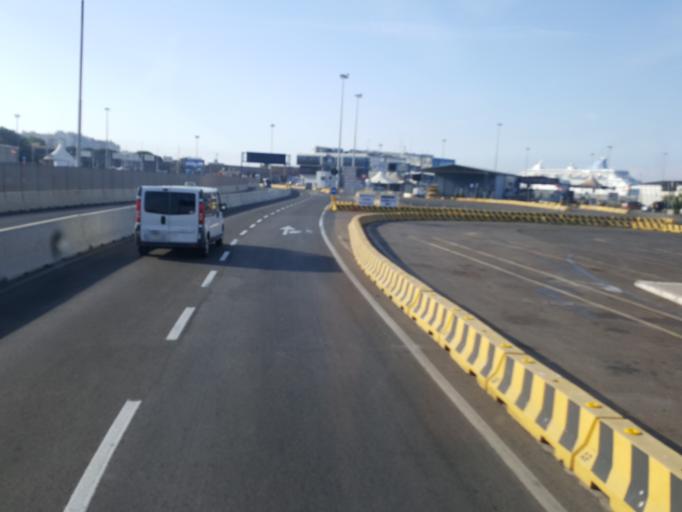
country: IT
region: Latium
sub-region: Citta metropolitana di Roma Capitale
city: Civitavecchia
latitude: 42.0989
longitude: 11.7849
